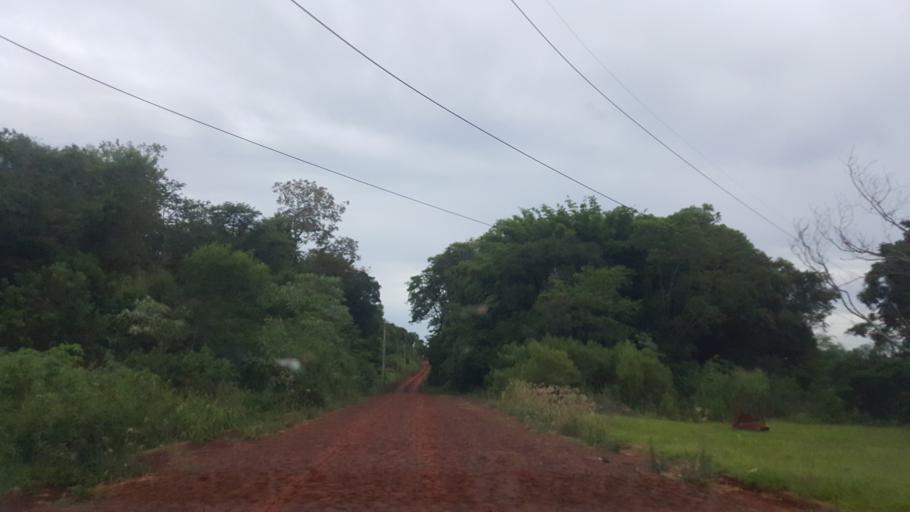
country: AR
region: Misiones
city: Capiovi
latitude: -26.9306
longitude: -55.0500
